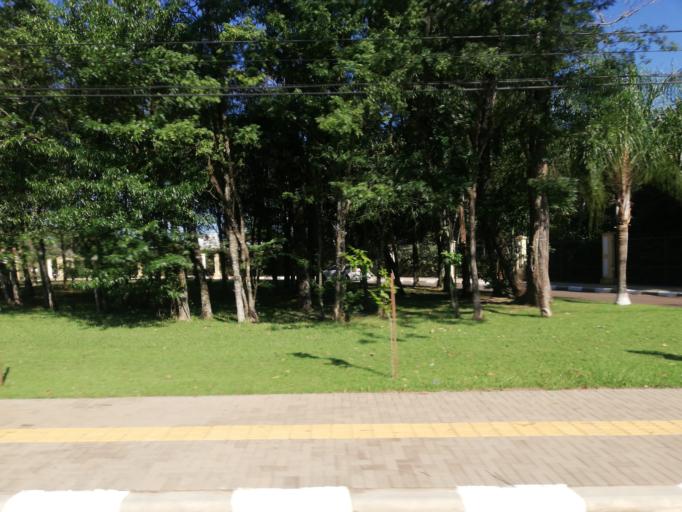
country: BR
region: Parana
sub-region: Foz Do Iguacu
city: Foz do Iguacu
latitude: -25.5581
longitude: -54.5635
